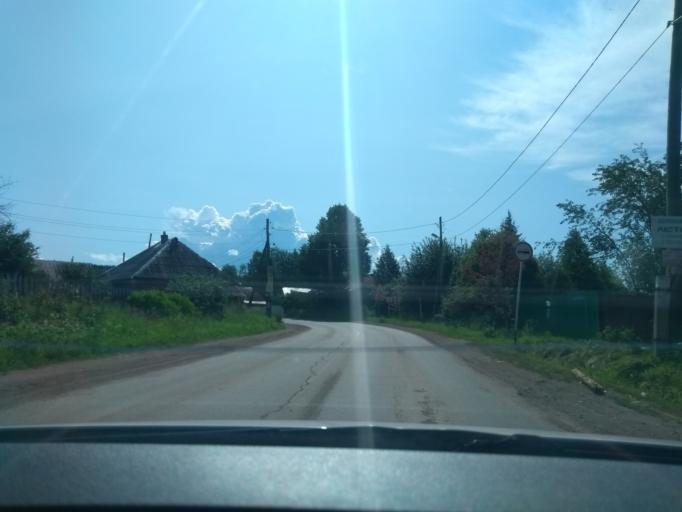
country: RU
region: Perm
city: Lobanovo
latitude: 57.8401
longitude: 56.3695
